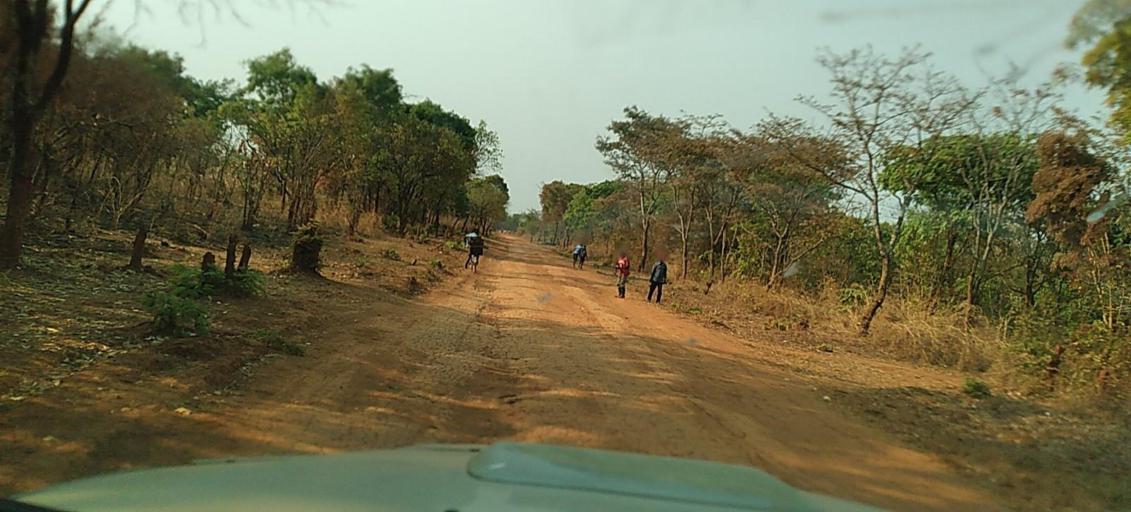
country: ZM
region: North-Western
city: Kasempa
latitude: -13.2990
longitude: 26.5541
